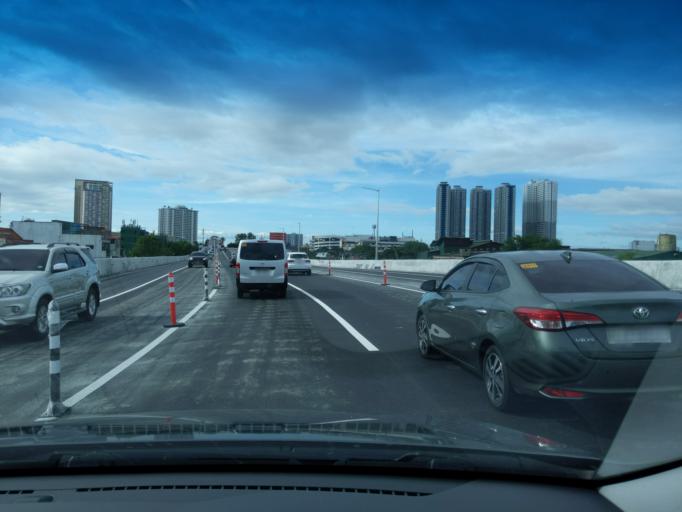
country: PH
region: Metro Manila
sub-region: San Juan
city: San Juan
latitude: 14.5996
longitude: 121.0234
